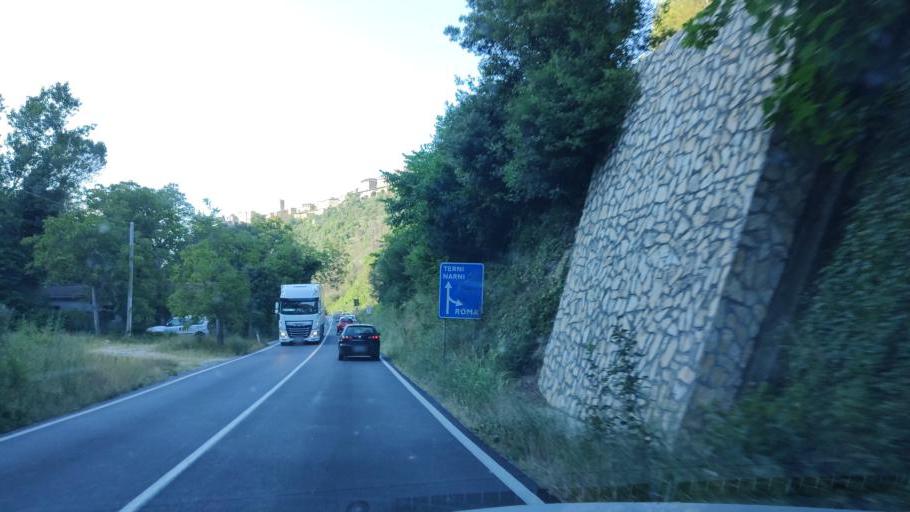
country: IT
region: Umbria
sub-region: Provincia di Terni
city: Narni
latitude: 42.5092
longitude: 12.5145
